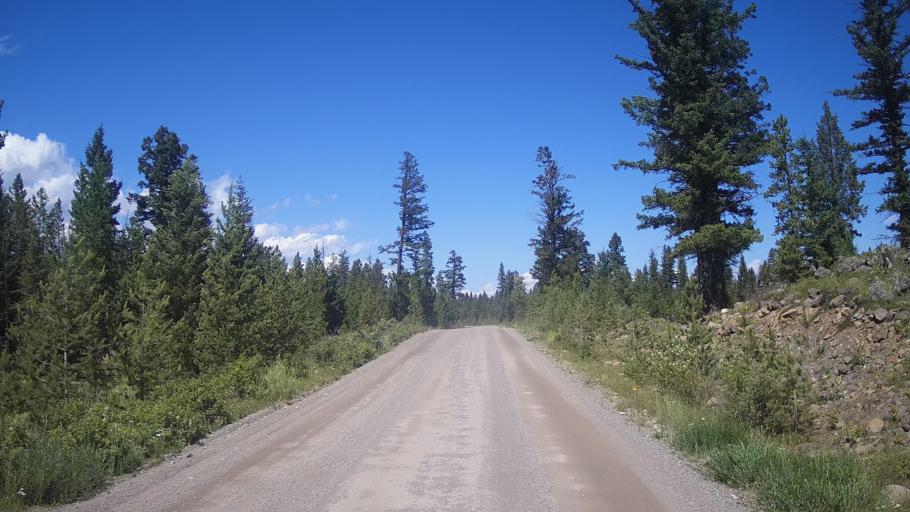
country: CA
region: British Columbia
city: Cache Creek
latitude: 51.1676
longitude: -121.5639
